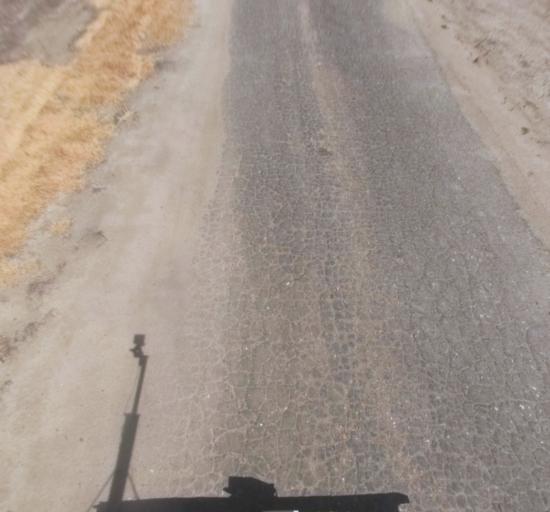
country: US
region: California
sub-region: Madera County
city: Chowchilla
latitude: 37.0439
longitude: -120.3468
